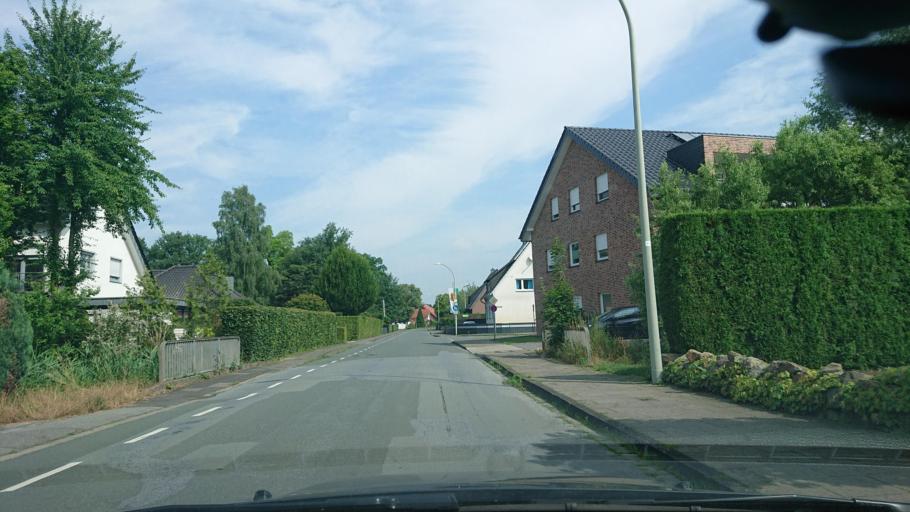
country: DE
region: North Rhine-Westphalia
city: Rietberg
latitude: 51.7515
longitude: 8.3931
